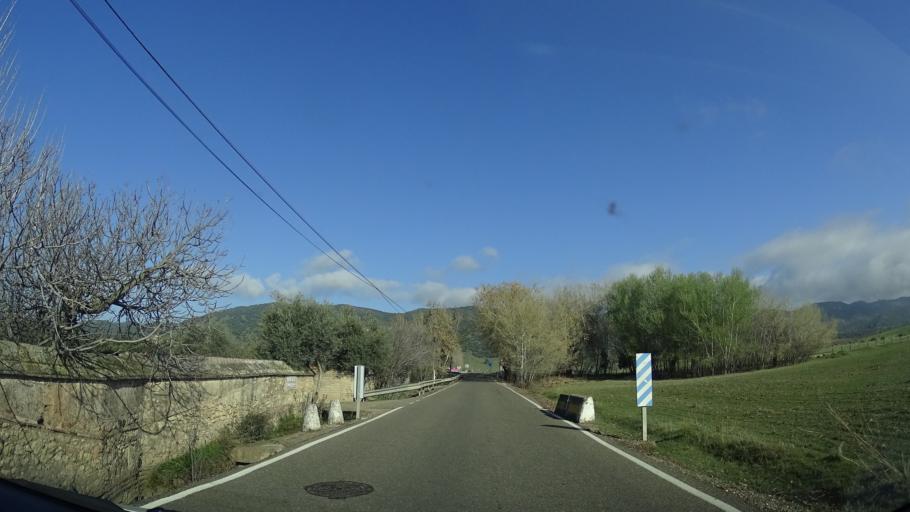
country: ES
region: Andalusia
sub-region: Province of Cordoba
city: Villarrubia
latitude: 37.8794
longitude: -4.8511
